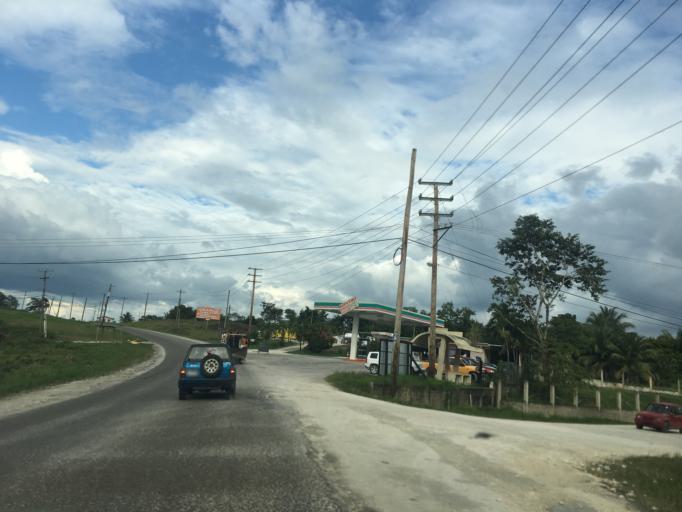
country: BZ
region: Cayo
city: San Ignacio
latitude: 17.1438
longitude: -89.0833
